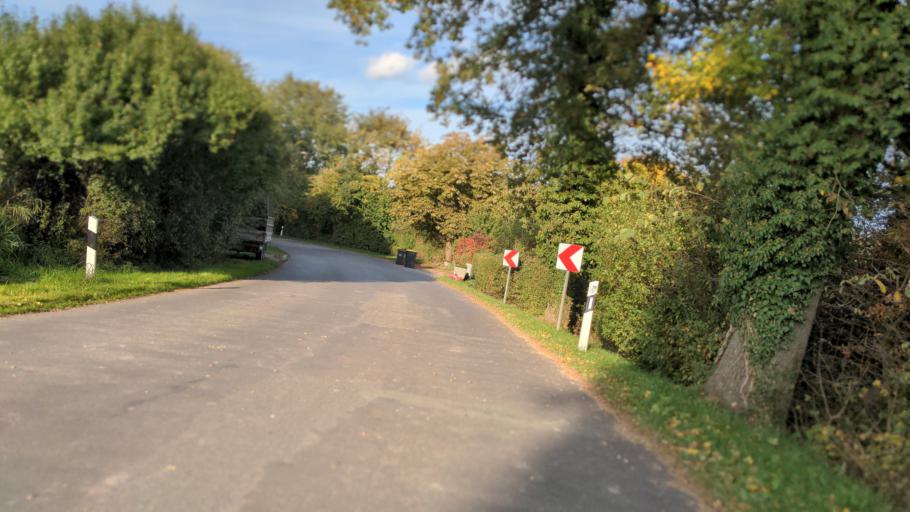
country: DE
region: Schleswig-Holstein
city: Pronstorf
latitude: 53.9596
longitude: 10.5274
